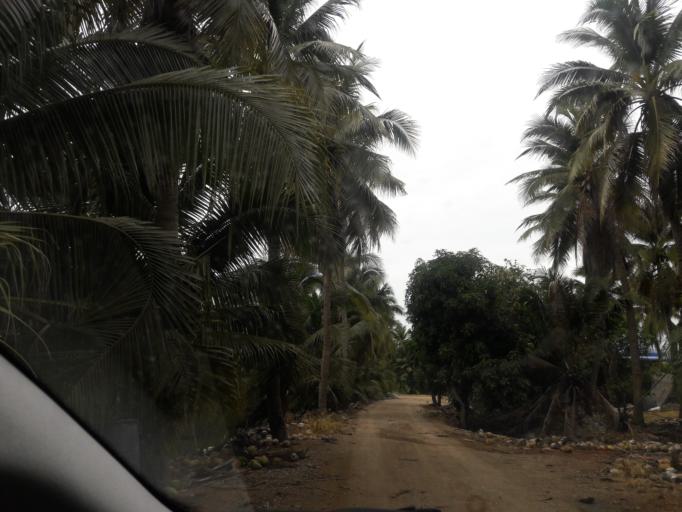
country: TH
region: Ratchaburi
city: Damnoen Saduak
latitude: 13.5374
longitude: 99.9327
